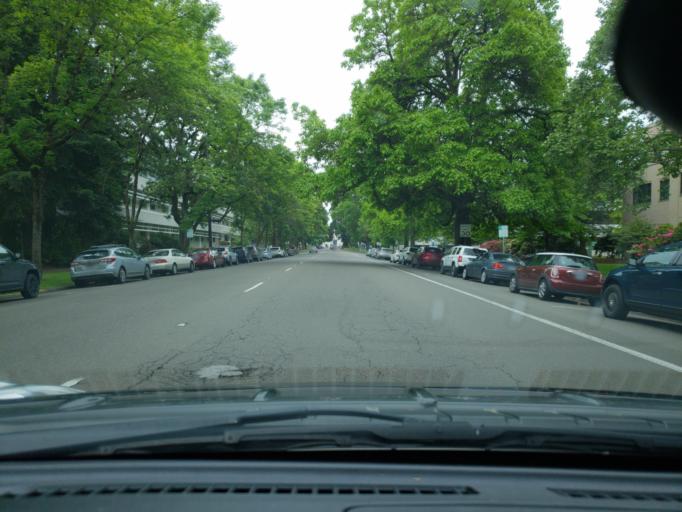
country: US
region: Oregon
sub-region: Marion County
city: Salem
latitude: 44.9454
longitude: -123.0270
